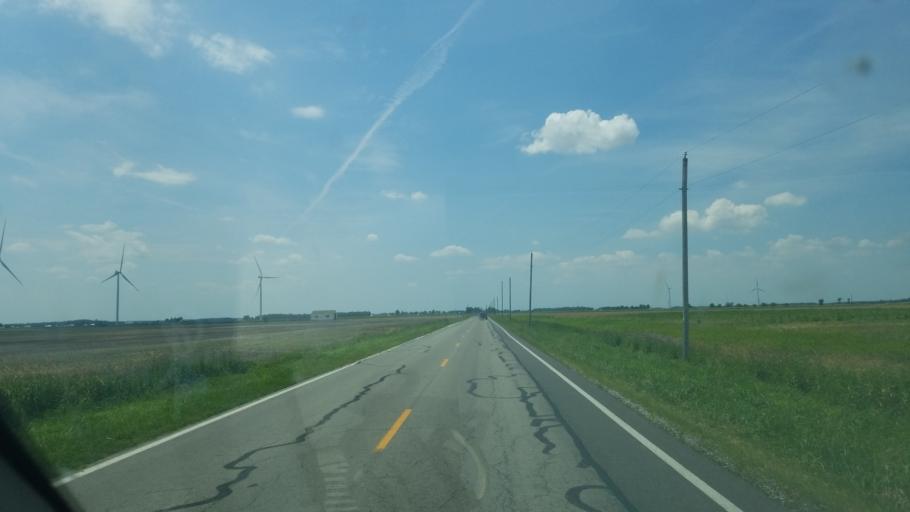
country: US
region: Ohio
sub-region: Hardin County
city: Ada
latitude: 40.7763
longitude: -83.7203
